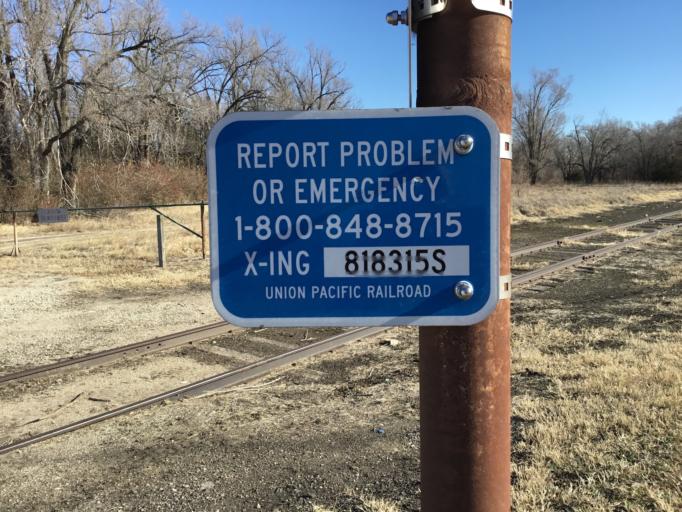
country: US
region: Kansas
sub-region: Geary County
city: Junction City
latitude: 39.0397
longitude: -96.8256
